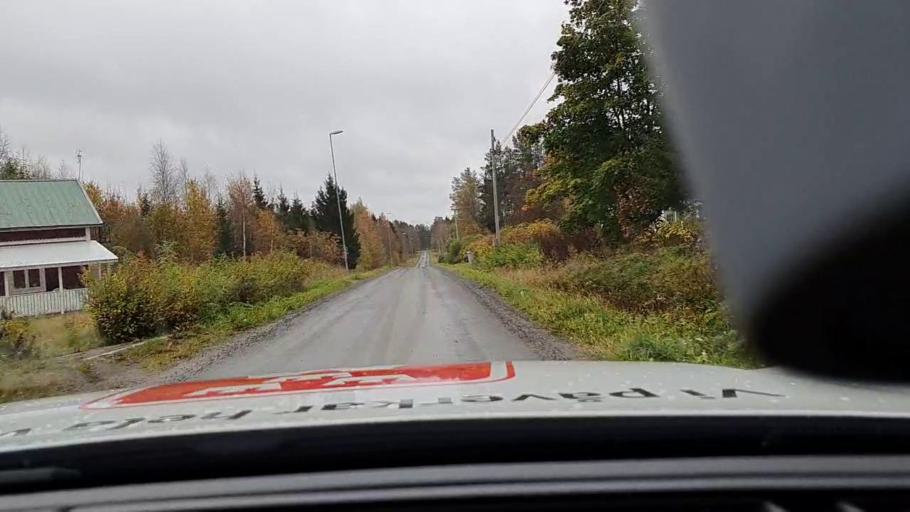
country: FI
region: Lapland
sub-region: Kemi-Tornio
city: Tornio
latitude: 65.9772
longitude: 24.0190
